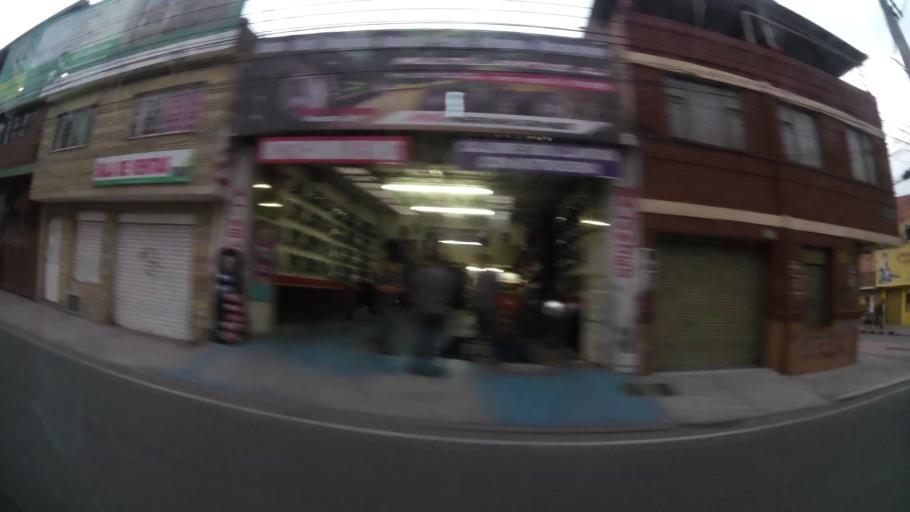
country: CO
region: Bogota D.C.
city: Bogota
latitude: 4.5874
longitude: -74.1271
